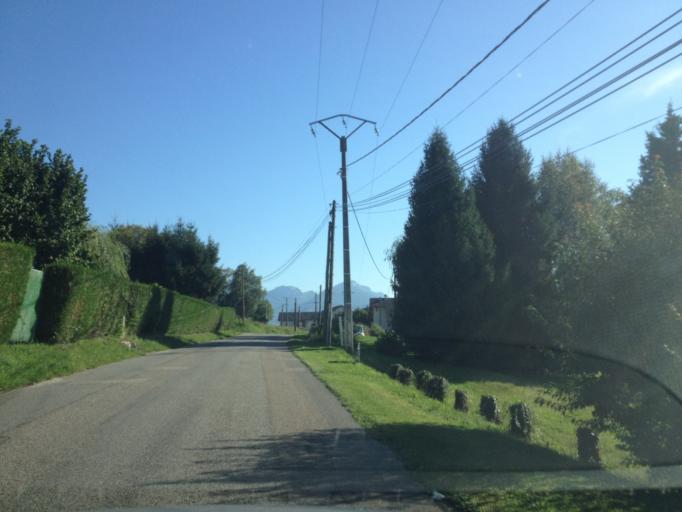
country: FR
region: Rhone-Alpes
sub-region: Departement de la Savoie
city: Sonnaz
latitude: 45.6188
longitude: 5.9058
